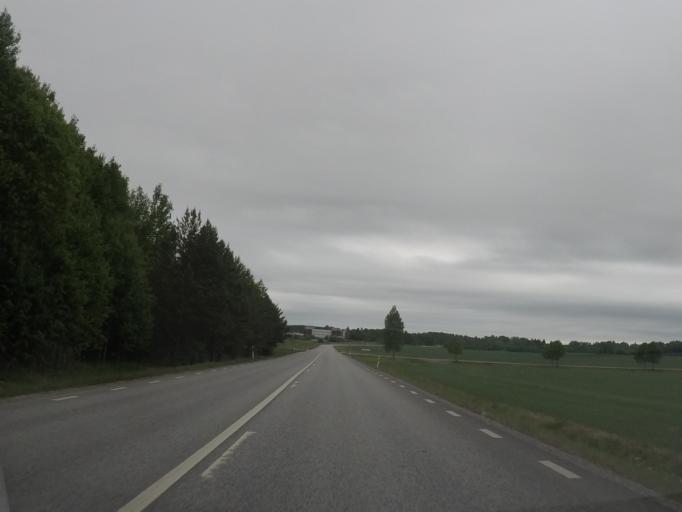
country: SE
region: Soedermanland
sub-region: Eskilstuna Kommun
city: Skogstorp
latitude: 59.2995
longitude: 16.4468
